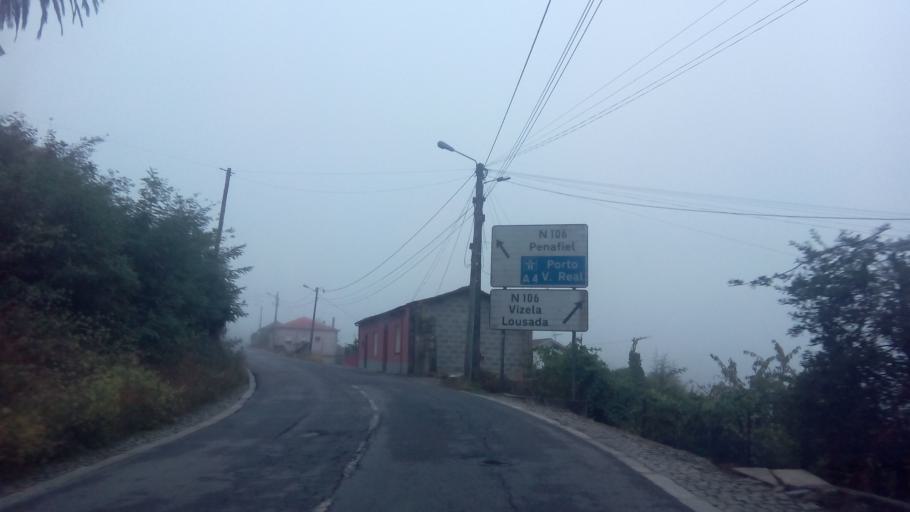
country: PT
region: Porto
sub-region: Penafiel
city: Penafiel
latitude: 41.2173
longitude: -8.2872
